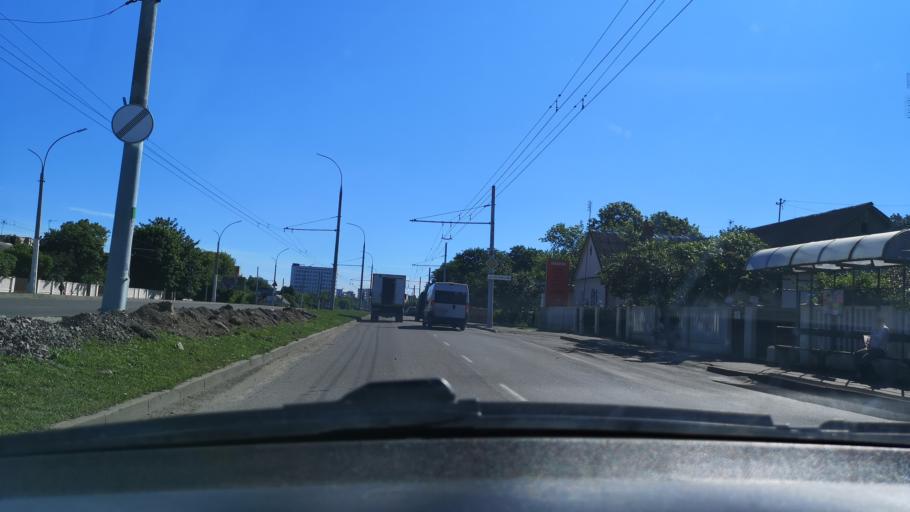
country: BY
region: Brest
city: Brest
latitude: 52.0914
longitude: 23.7221
